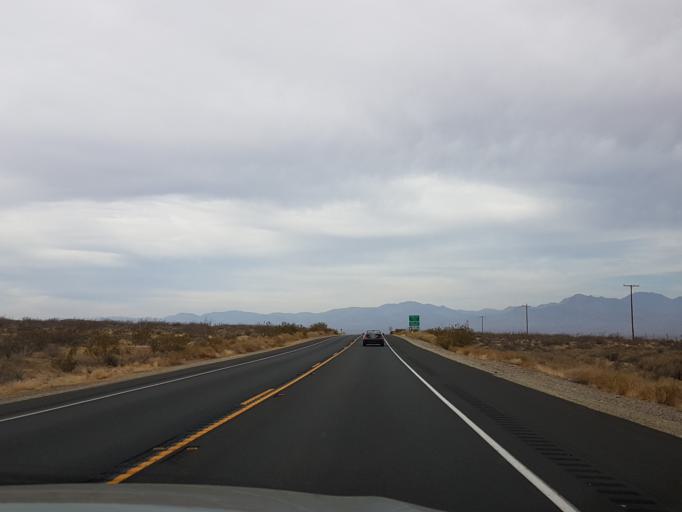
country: US
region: California
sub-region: Kern County
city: Ridgecrest
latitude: 35.5473
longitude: -117.7036
